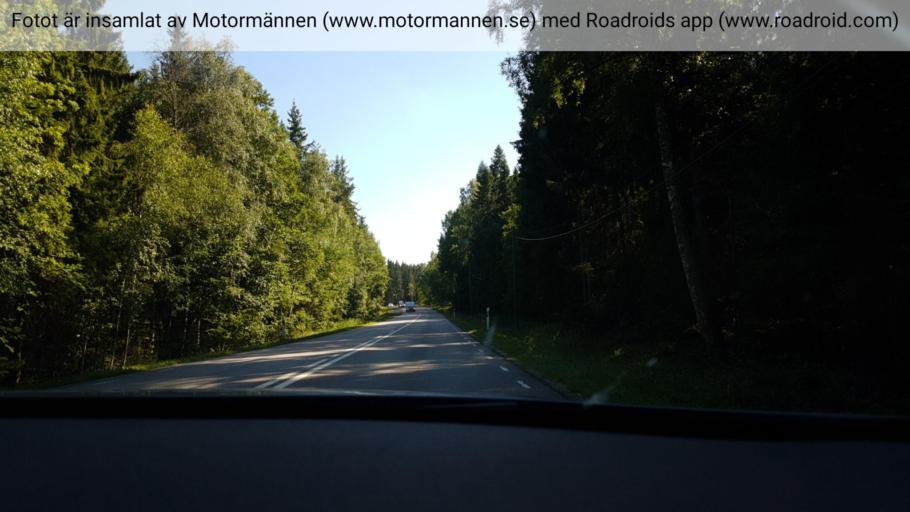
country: SE
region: Vaestra Goetaland
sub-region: Skara Kommun
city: Skara
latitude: 58.3255
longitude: 13.4358
